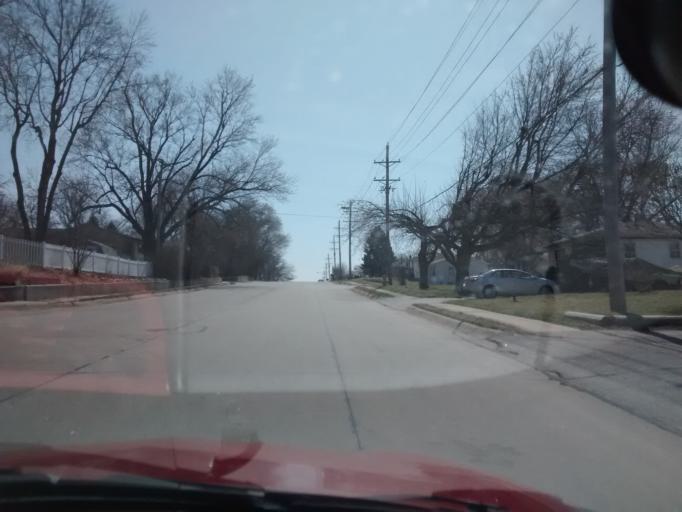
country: US
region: Nebraska
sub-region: Sarpy County
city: Bellevue
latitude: 41.1446
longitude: -95.9075
